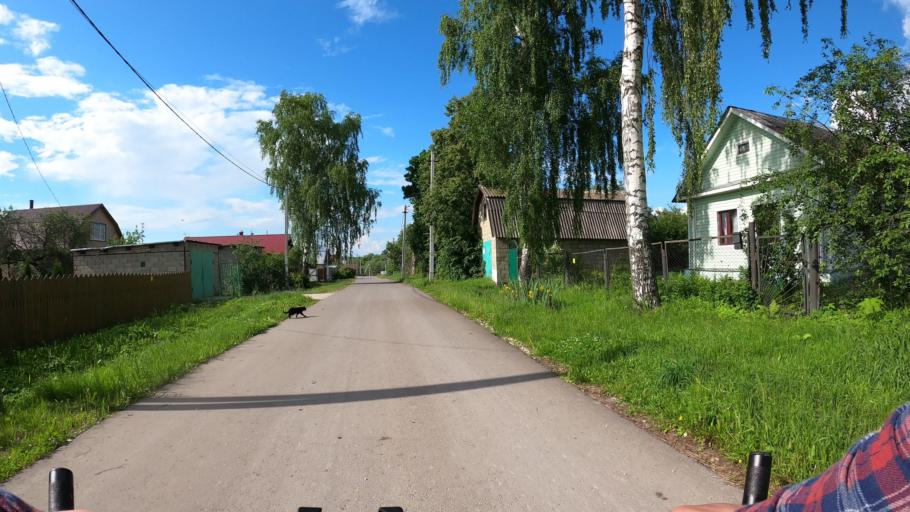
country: RU
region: Moskovskaya
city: Konobeyevo
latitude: 55.4204
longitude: 38.6502
